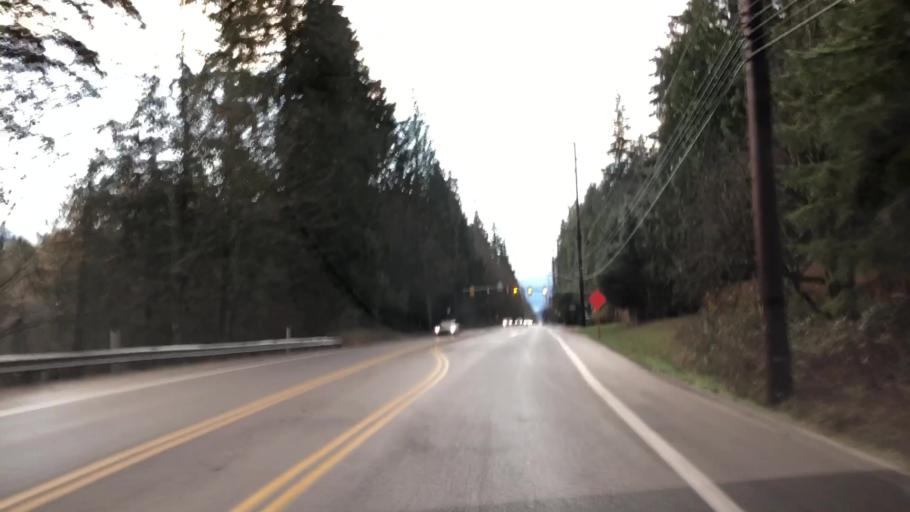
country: US
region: Washington
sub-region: King County
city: City of Sammamish
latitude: 47.6329
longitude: -122.0354
